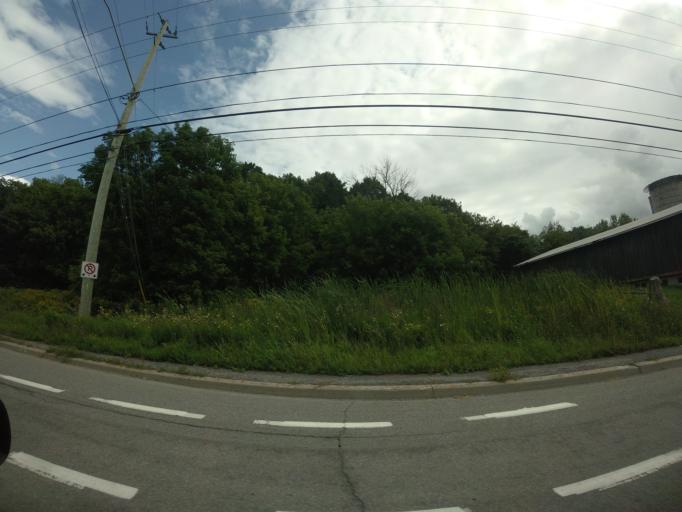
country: CA
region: Quebec
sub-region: Outaouais
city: Gatineau
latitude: 45.4607
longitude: -75.5515
